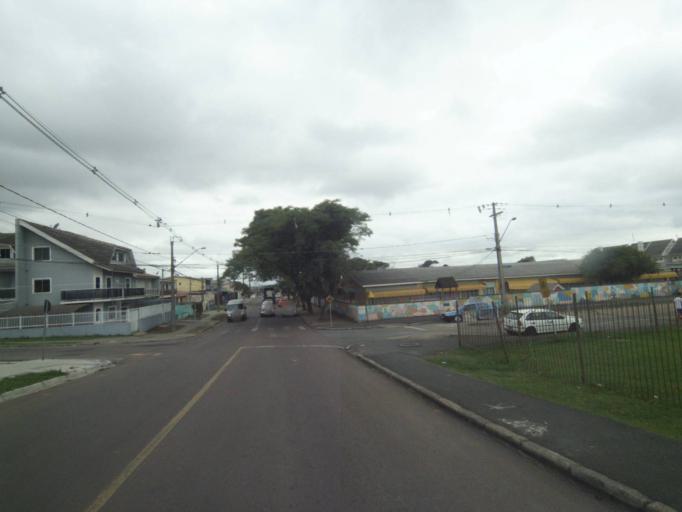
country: BR
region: Parana
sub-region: Sao Jose Dos Pinhais
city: Sao Jose dos Pinhais
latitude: -25.5445
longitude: -49.2841
